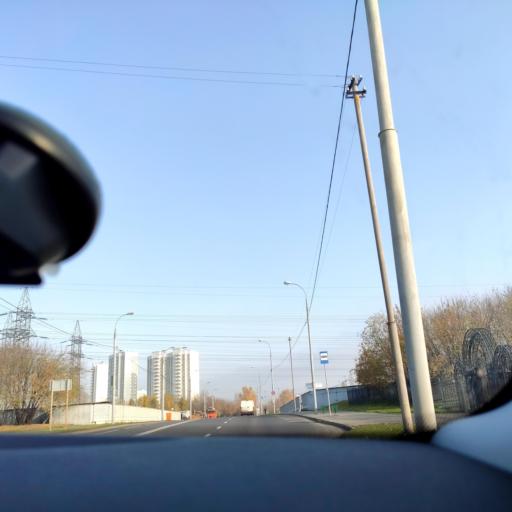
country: RU
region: Moscow
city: Kuz'minki
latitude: 55.6731
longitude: 37.7963
